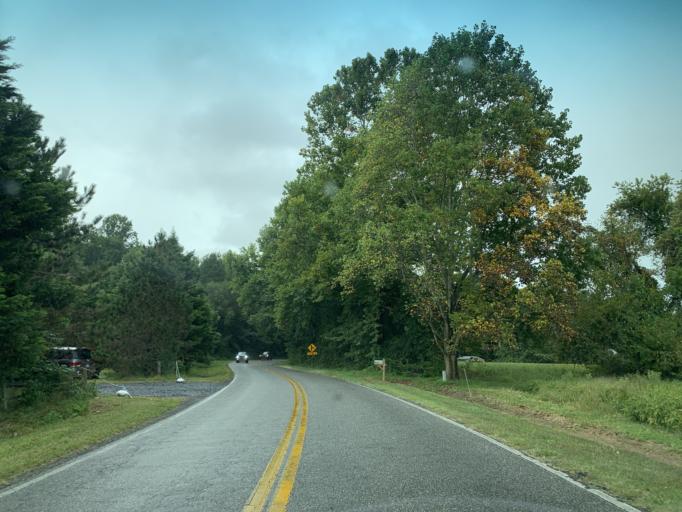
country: US
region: Maryland
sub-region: Caroline County
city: Denton
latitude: 38.9117
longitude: -75.8538
